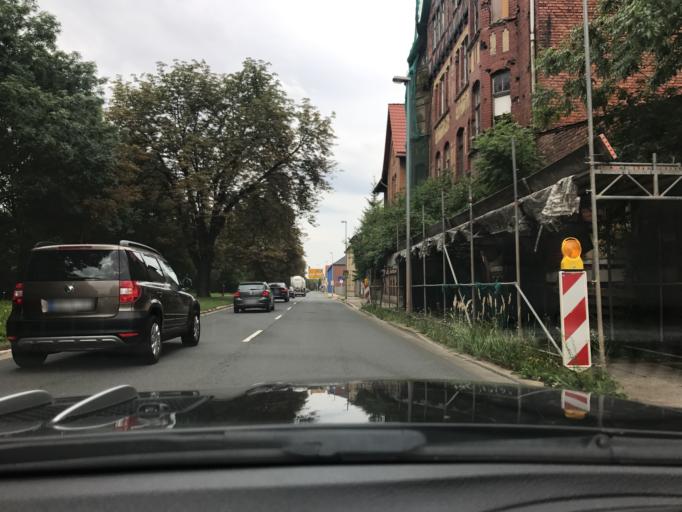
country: DE
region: Thuringia
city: Nordhausen
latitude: 51.4944
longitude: 10.7968
